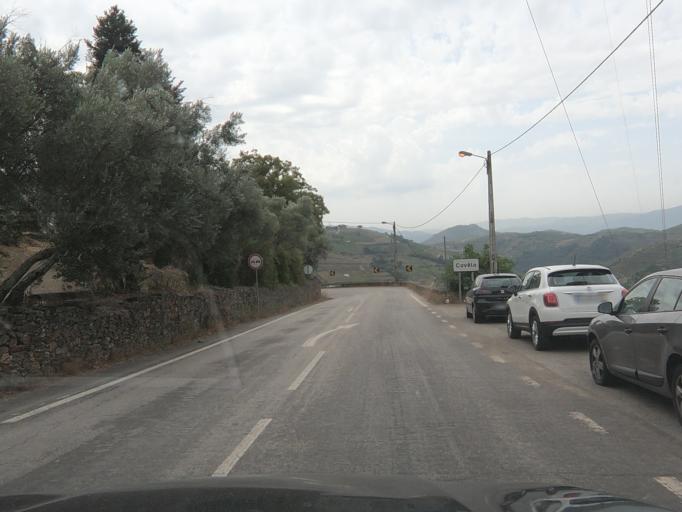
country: PT
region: Vila Real
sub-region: Santa Marta de Penaguiao
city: Santa Marta de Penaguiao
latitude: 41.2404
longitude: -7.7671
